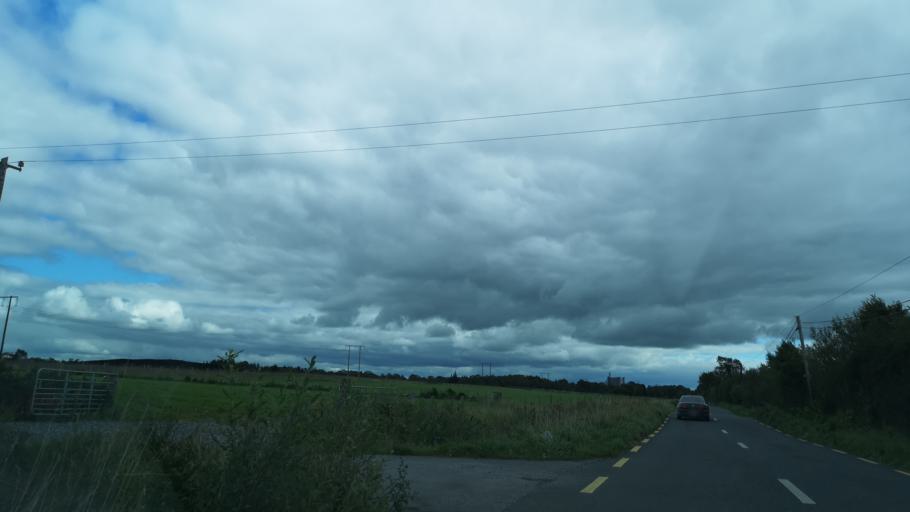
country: IE
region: Leinster
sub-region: Uibh Fhaili
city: Banagher
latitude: 53.2846
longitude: -8.0759
